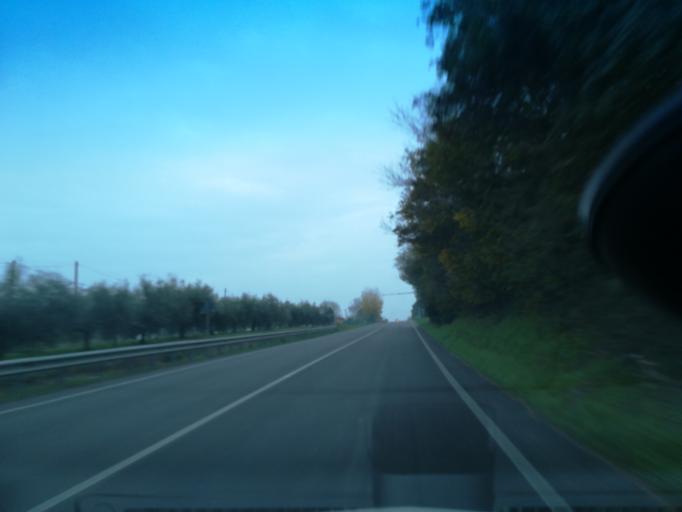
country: IT
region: Emilia-Romagna
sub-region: Provincia di Ravenna
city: Castel Bolognese
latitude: 44.3325
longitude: 11.7672
